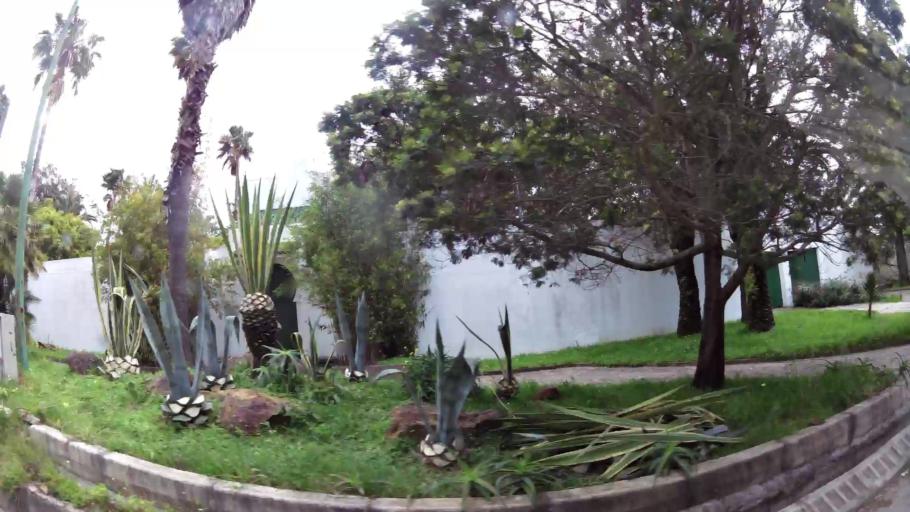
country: MA
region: Tanger-Tetouan
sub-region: Tanger-Assilah
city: Tangier
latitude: 35.7845
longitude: -5.8491
